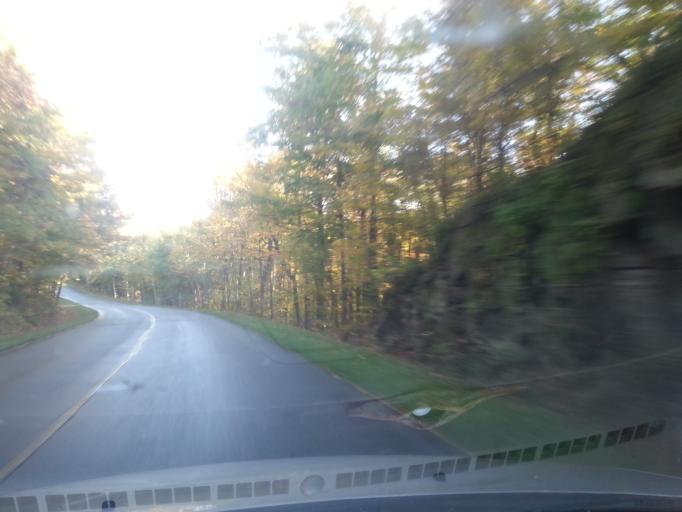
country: CA
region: Quebec
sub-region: Outaouais
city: Gatineau
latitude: 45.4818
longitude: -75.8559
